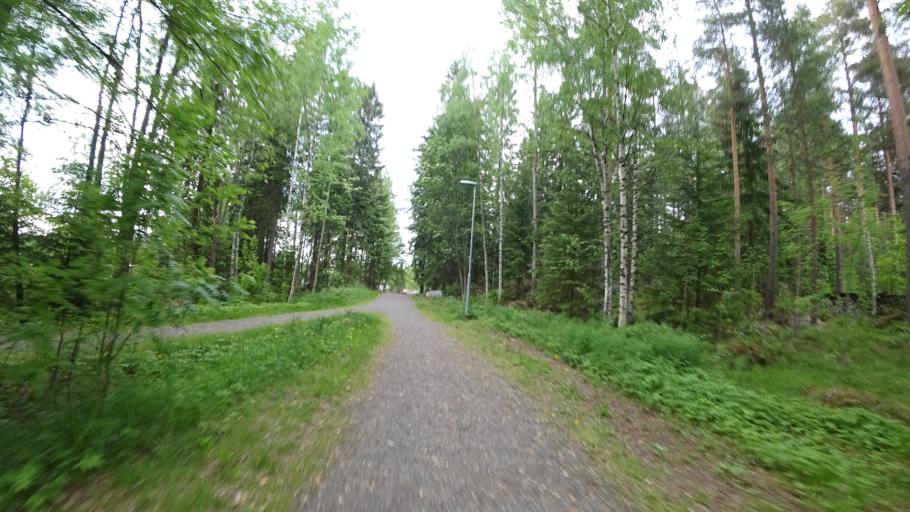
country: FI
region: Pirkanmaa
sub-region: Tampere
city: Yloejaervi
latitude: 61.5202
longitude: 23.6068
